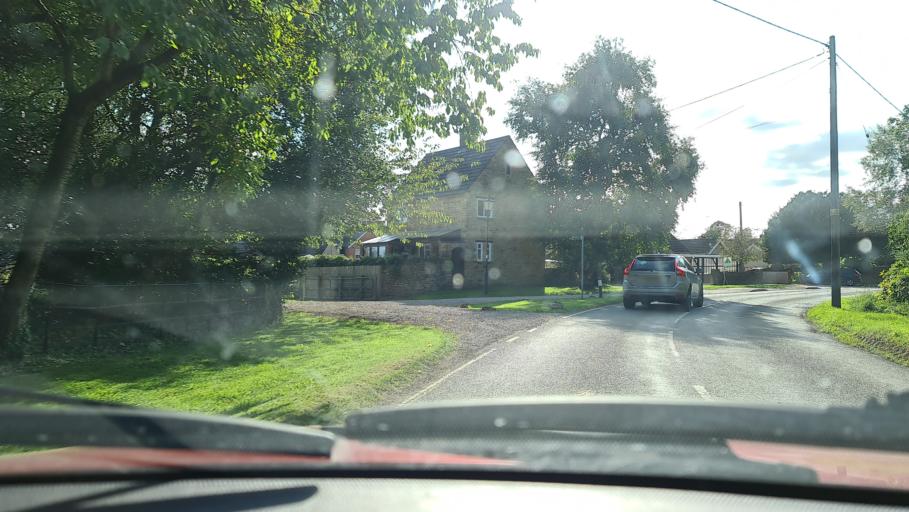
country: GB
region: England
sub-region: Oxfordshire
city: Adderbury
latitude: 52.0239
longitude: -1.2652
